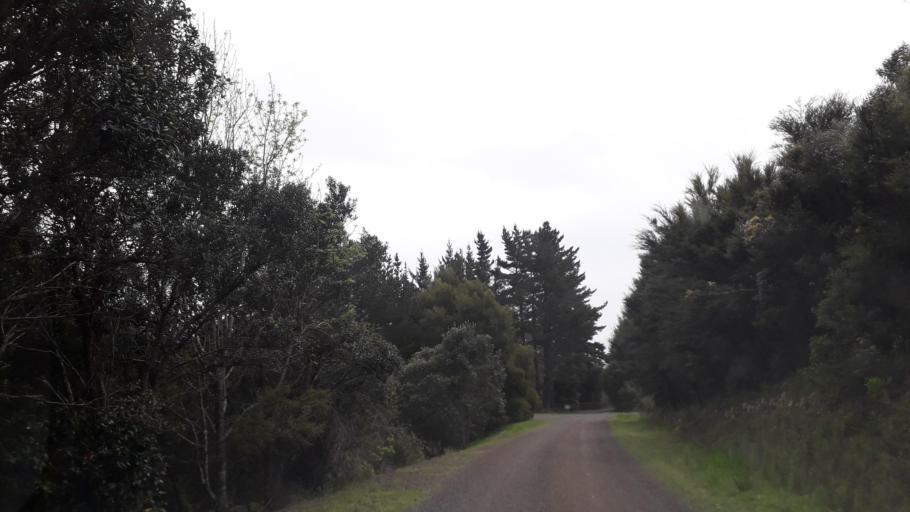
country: NZ
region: Northland
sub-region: Far North District
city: Paihia
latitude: -35.2808
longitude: 174.1837
